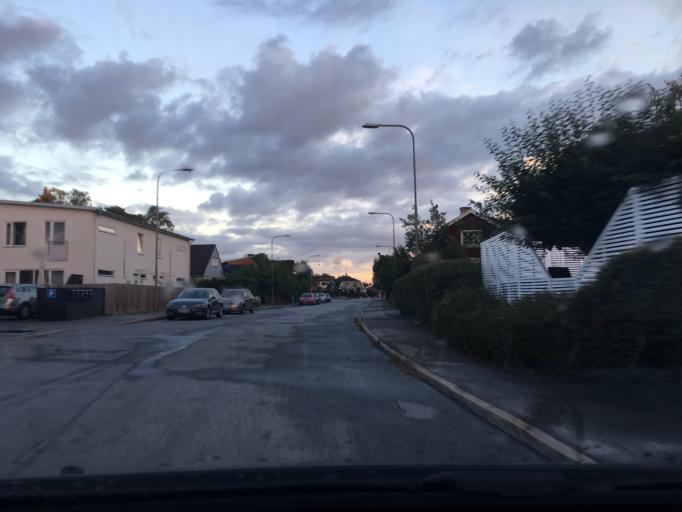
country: SE
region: Stockholm
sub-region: Jarfalla Kommun
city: Jakobsberg
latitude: 59.3760
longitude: 17.8766
